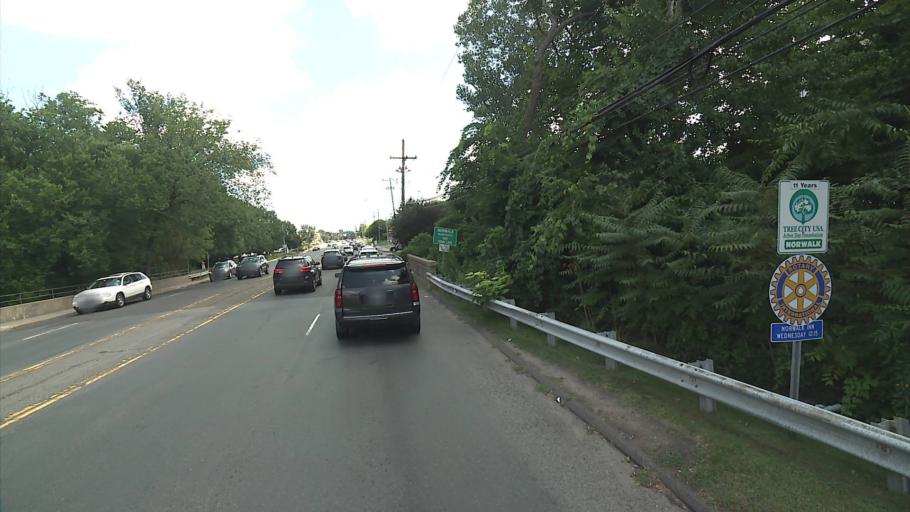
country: US
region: Connecticut
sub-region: Fairfield County
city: Darien
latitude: 41.0918
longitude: -73.4537
